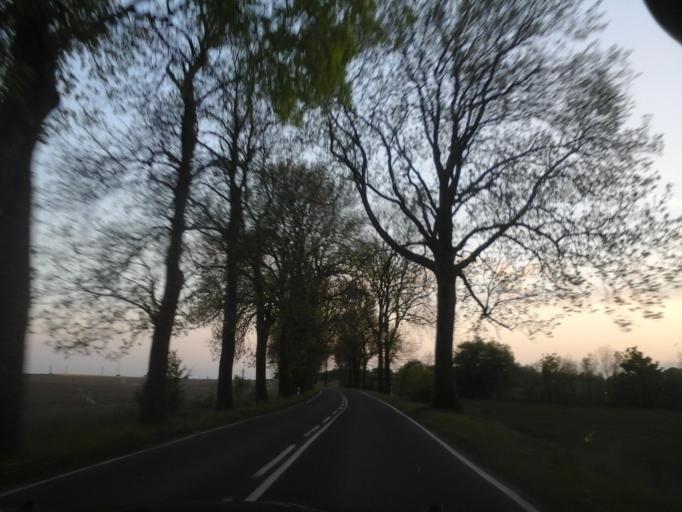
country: PL
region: West Pomeranian Voivodeship
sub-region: Powiat choszczenski
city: Choszczno
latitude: 53.1928
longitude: 15.4374
